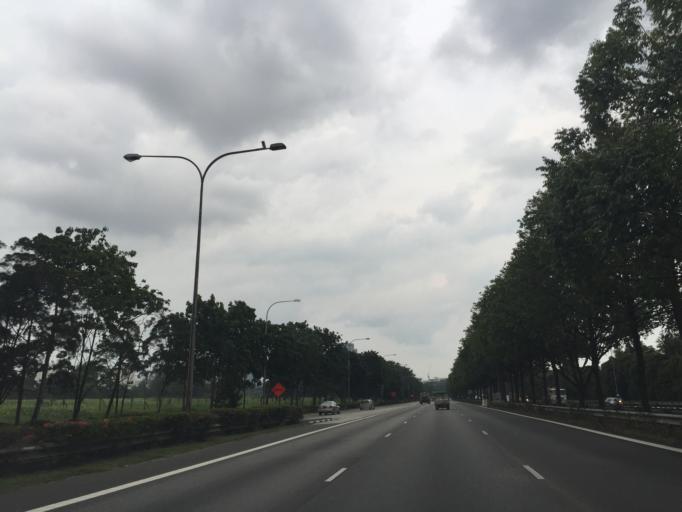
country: SG
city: Singapore
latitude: 1.3256
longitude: 103.7281
